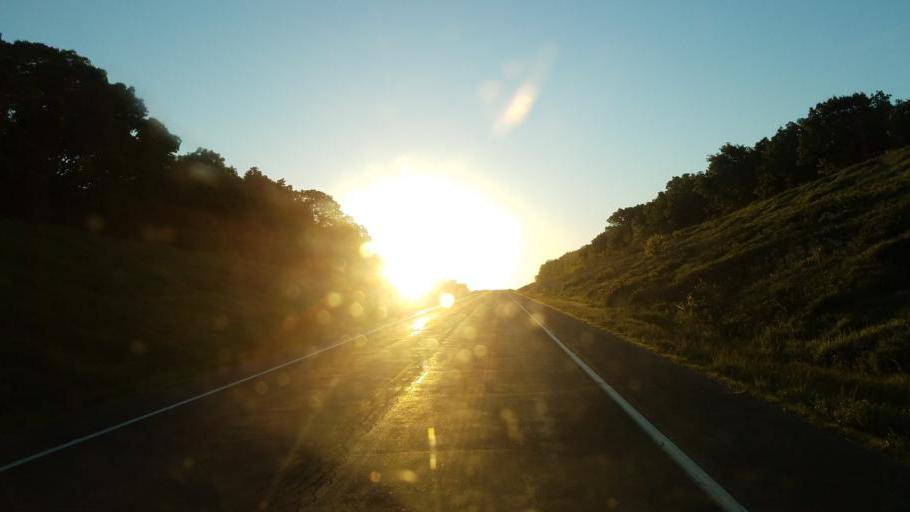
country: US
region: Missouri
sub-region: Schuyler County
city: Lancaster
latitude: 40.4891
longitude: -92.6188
